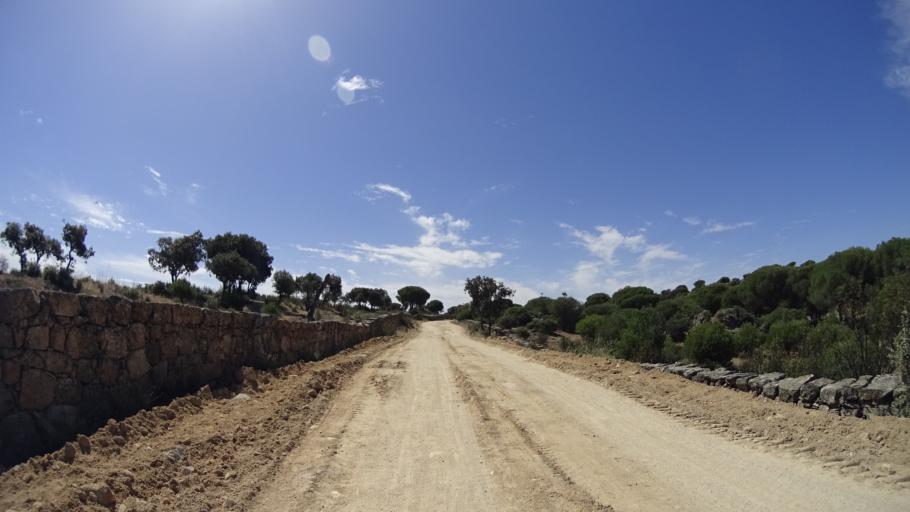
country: ES
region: Madrid
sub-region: Provincia de Madrid
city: Torrelodones
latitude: 40.5665
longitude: -3.9387
